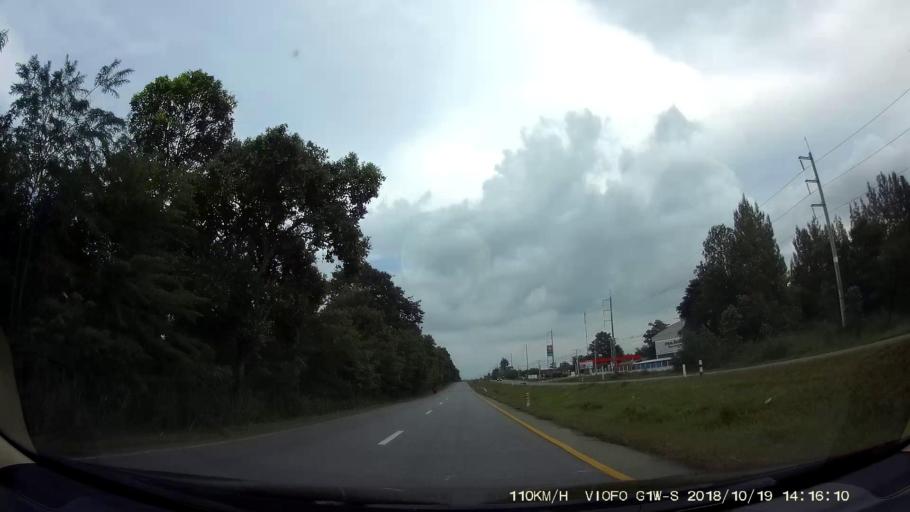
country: TH
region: Chaiyaphum
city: Khon Sawan
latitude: 15.9912
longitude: 102.2080
